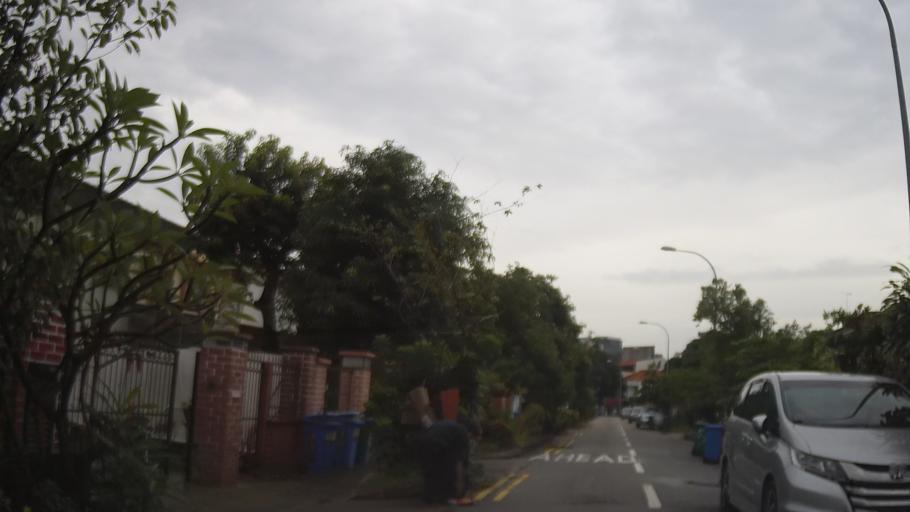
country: SG
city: Singapore
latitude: 1.3293
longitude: 103.8808
